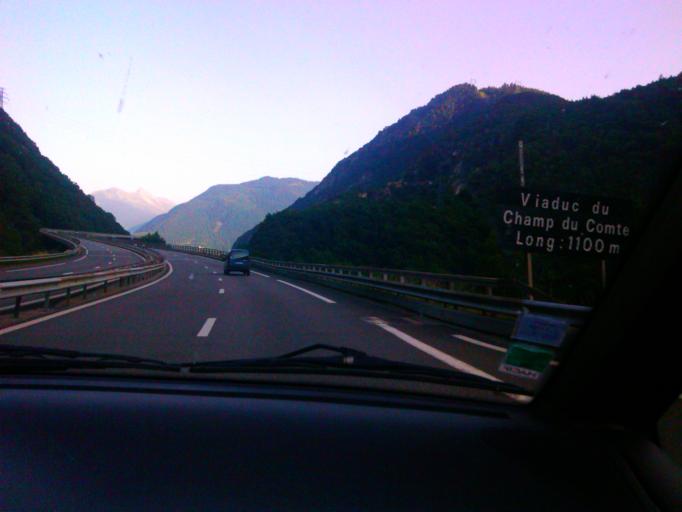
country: FR
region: Rhone-Alpes
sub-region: Departement de la Savoie
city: La Bathie
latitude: 45.5831
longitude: 6.4562
